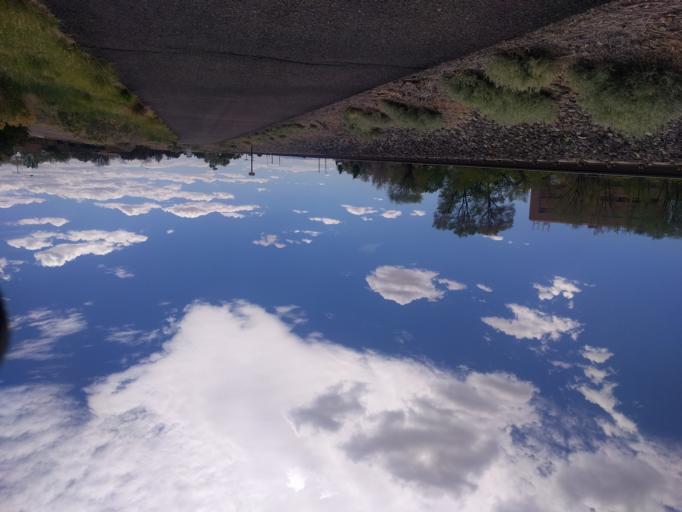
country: US
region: New Mexico
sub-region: Santa Fe County
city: Santa Fe
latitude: 35.6410
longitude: -105.9616
